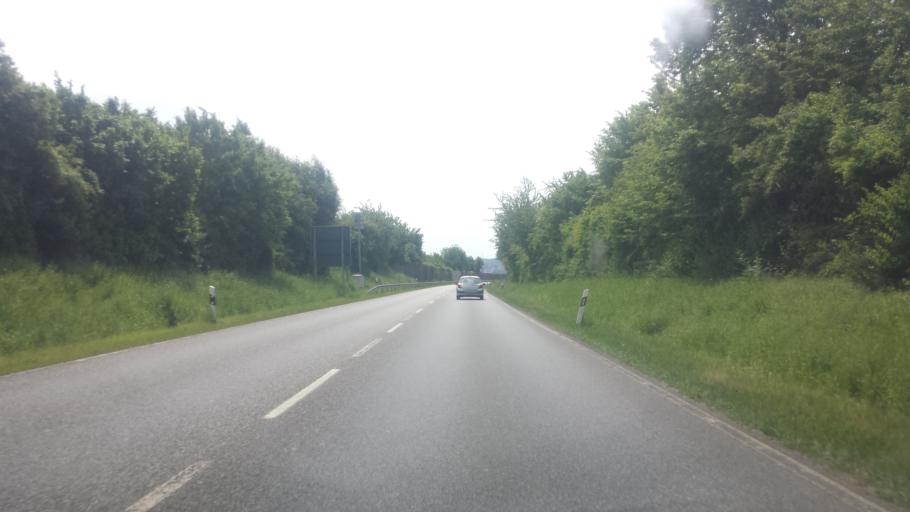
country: DE
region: Hesse
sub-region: Regierungsbezirk Darmstadt
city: Bad Vilbel
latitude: 50.2073
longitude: 8.7359
